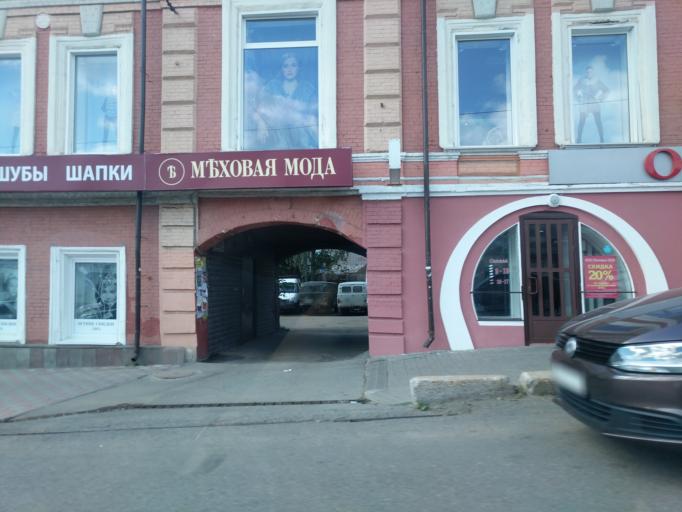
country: RU
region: Kirov
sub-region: Kirovo-Chepetskiy Rayon
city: Kirov
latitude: 58.6027
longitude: 49.6809
